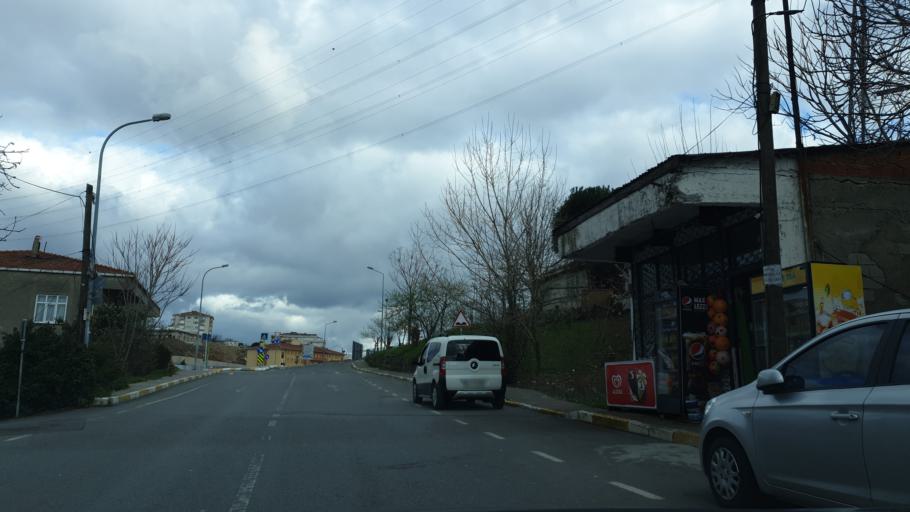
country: TR
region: Istanbul
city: Pendik
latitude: 40.8983
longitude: 29.2420
